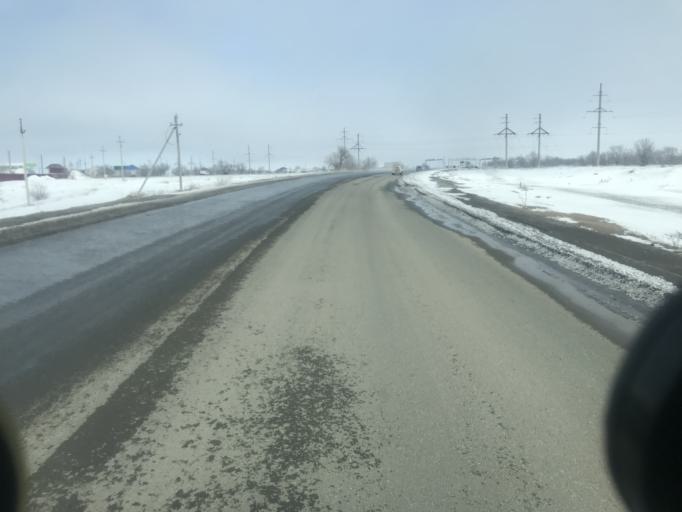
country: KZ
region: Aqtoebe
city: Aqtobe
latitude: 50.2873
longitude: 57.2861
